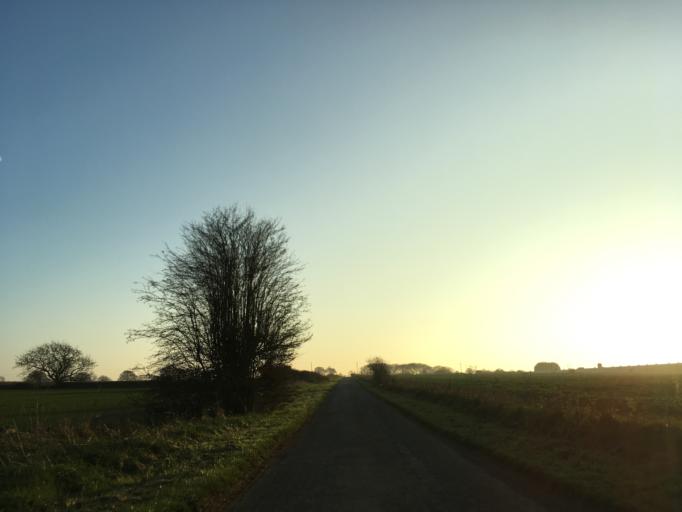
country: GB
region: England
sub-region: South Gloucestershire
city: Marshfield
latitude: 51.4688
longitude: -2.2983
